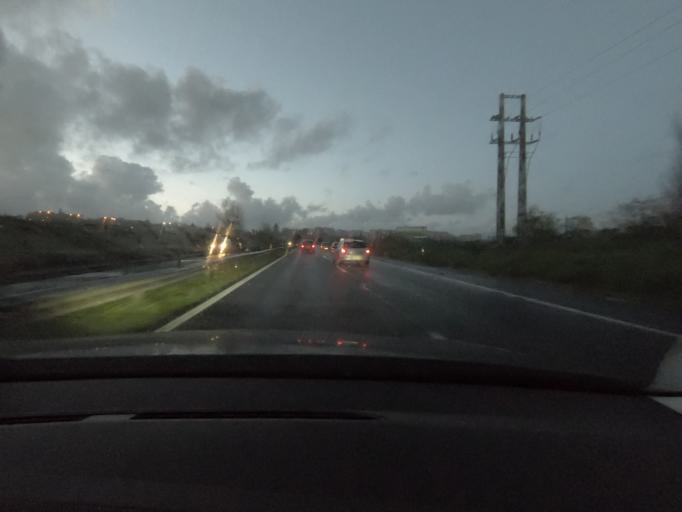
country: PT
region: Lisbon
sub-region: Oeiras
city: Barcarena
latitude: 38.7371
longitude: -9.2987
